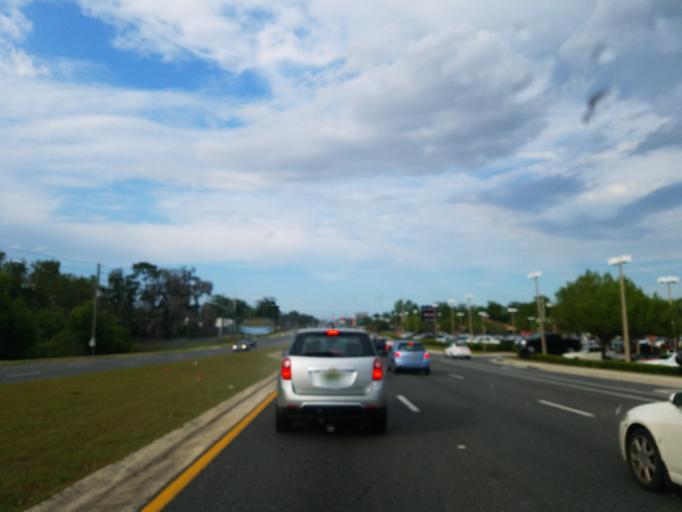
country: US
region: Florida
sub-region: Marion County
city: Ocala
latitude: 29.1434
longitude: -82.1919
